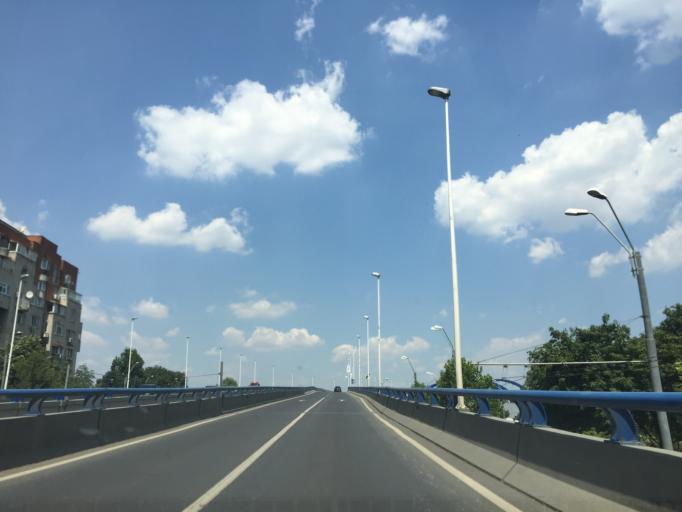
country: RO
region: Bucuresti
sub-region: Municipiul Bucuresti
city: Bucharest
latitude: 44.4059
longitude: 26.1213
